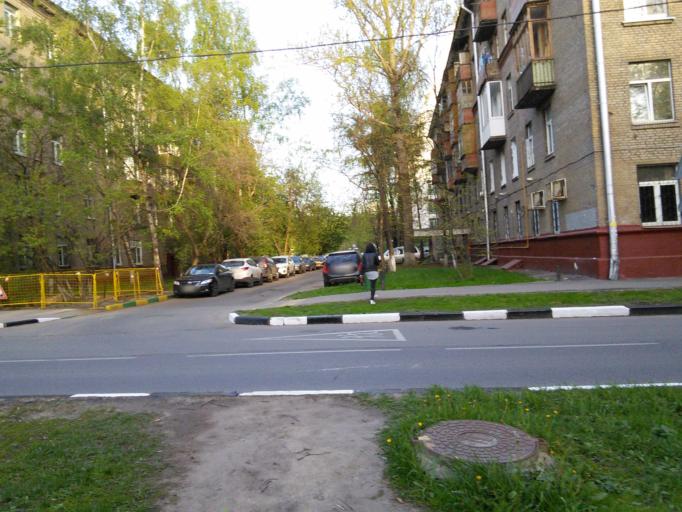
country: RU
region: Moscow
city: Novyye Cheremushki
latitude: 55.6859
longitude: 37.5837
